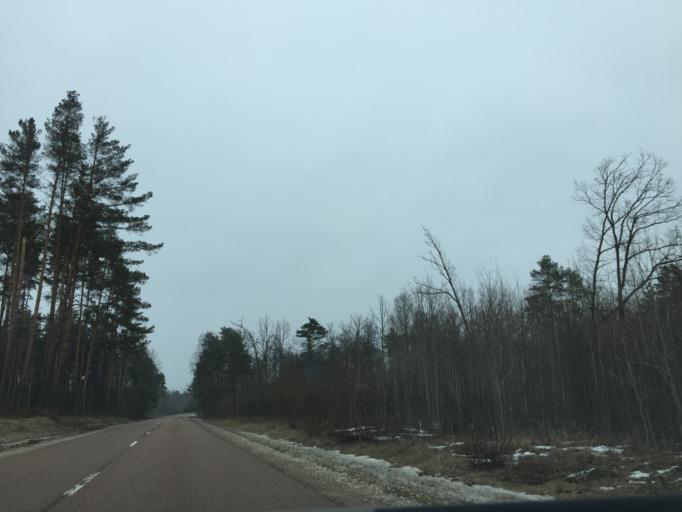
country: LV
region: Olaine
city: Olaine
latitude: 56.6365
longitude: 23.9361
